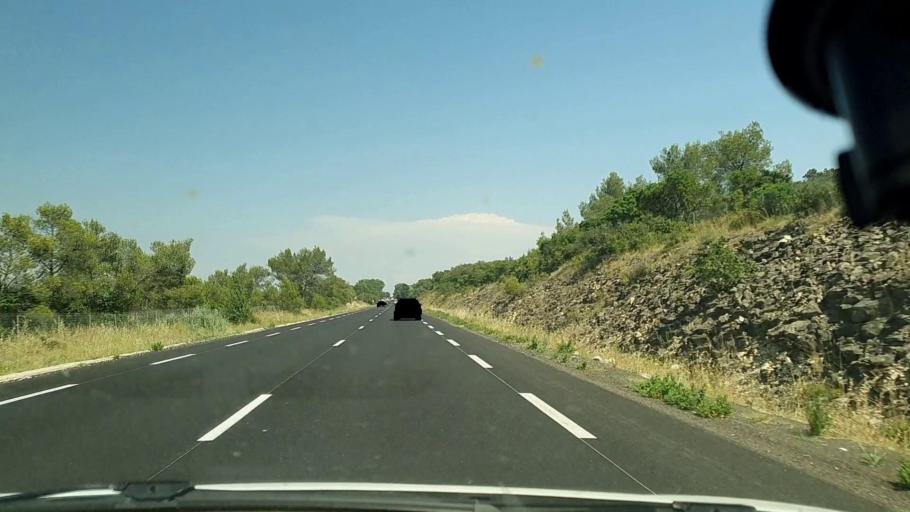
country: FR
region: Languedoc-Roussillon
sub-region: Departement du Gard
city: Clarensac
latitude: 43.8579
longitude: 4.2336
